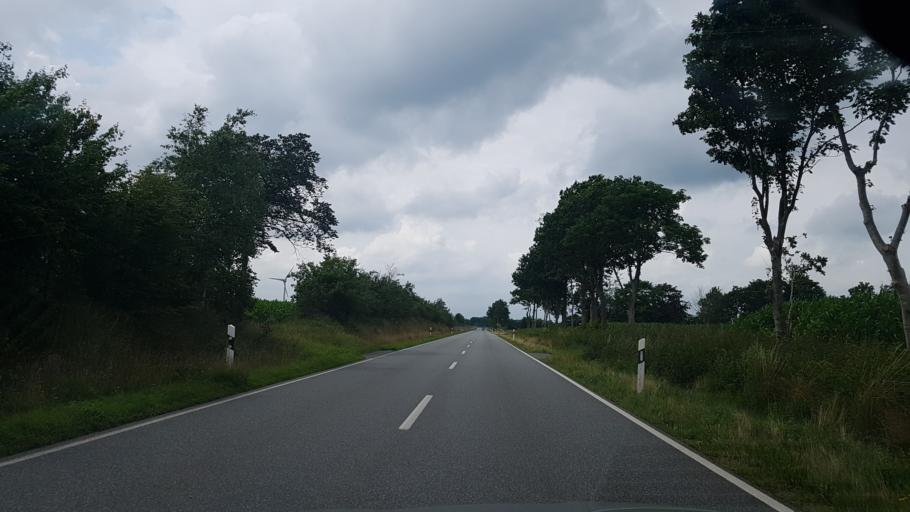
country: DE
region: Schleswig-Holstein
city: Boxlund
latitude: 54.8579
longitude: 9.1632
